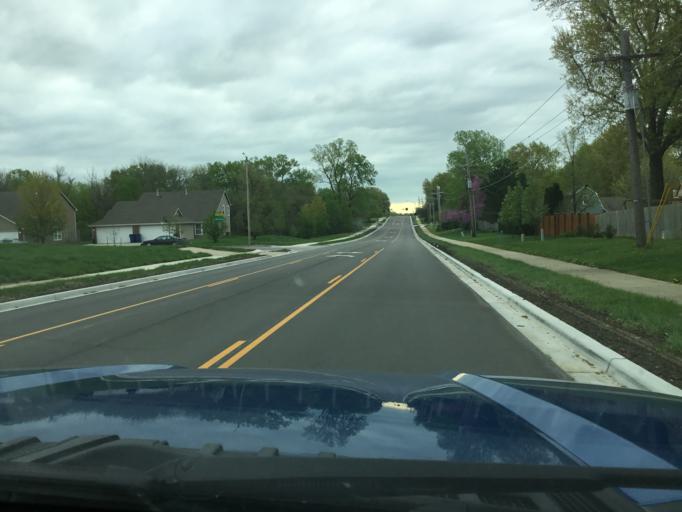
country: US
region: Kansas
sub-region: Douglas County
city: Lawrence
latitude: 38.9861
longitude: -95.2743
